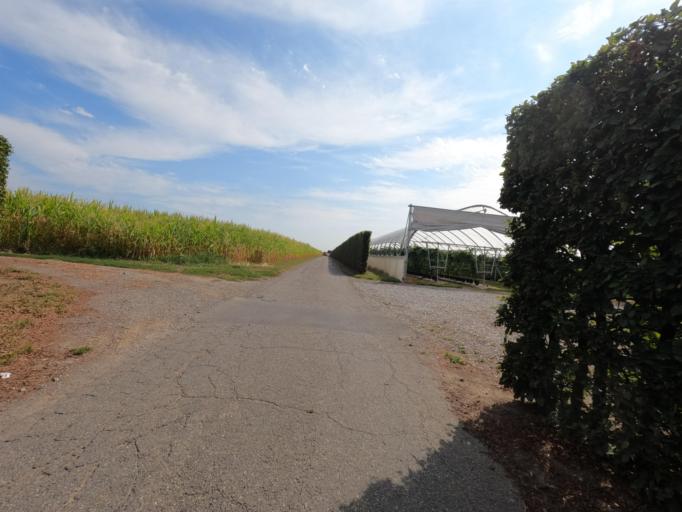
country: DE
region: North Rhine-Westphalia
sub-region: Regierungsbezirk Koln
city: Waldfeucht
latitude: 51.0597
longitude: 6.0310
